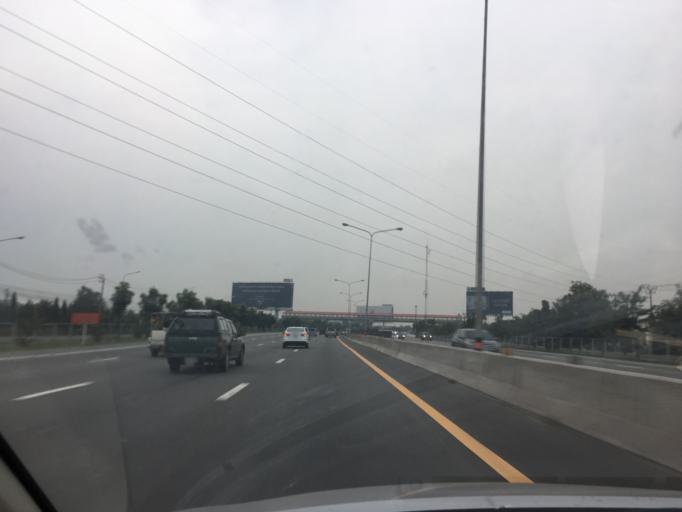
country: TH
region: Bangkok
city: Bang Na
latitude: 13.6719
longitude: 100.6992
